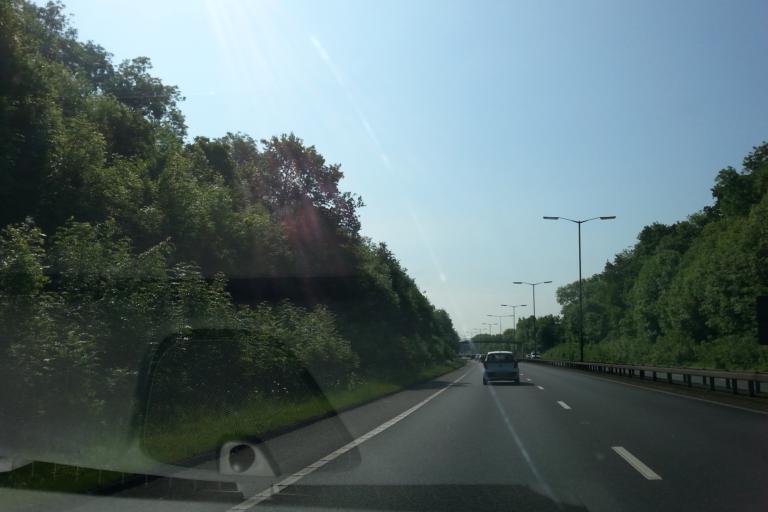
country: GB
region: England
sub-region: Peterborough
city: Marholm
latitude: 52.5696
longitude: -0.2935
